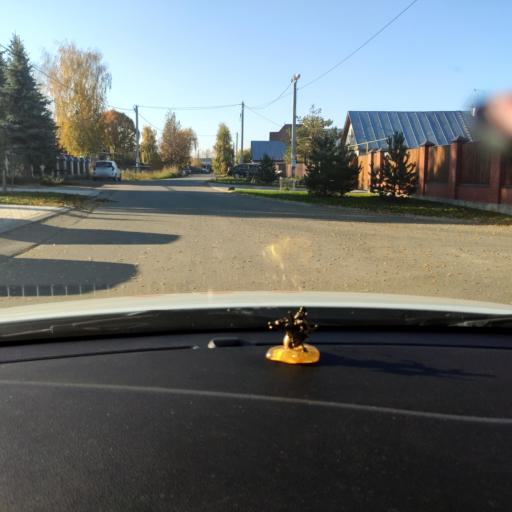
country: RU
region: Tatarstan
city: Stolbishchi
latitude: 55.6246
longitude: 49.1530
